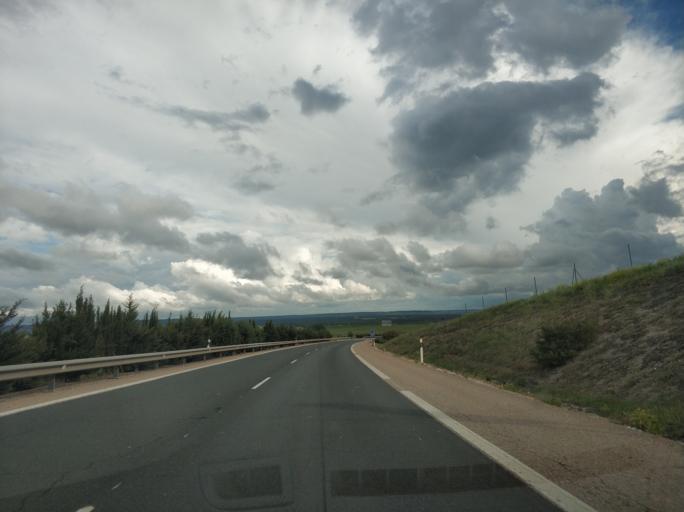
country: ES
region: Castille and Leon
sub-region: Provincia de Valladolid
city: Cisterniga
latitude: 41.6066
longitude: -4.6652
